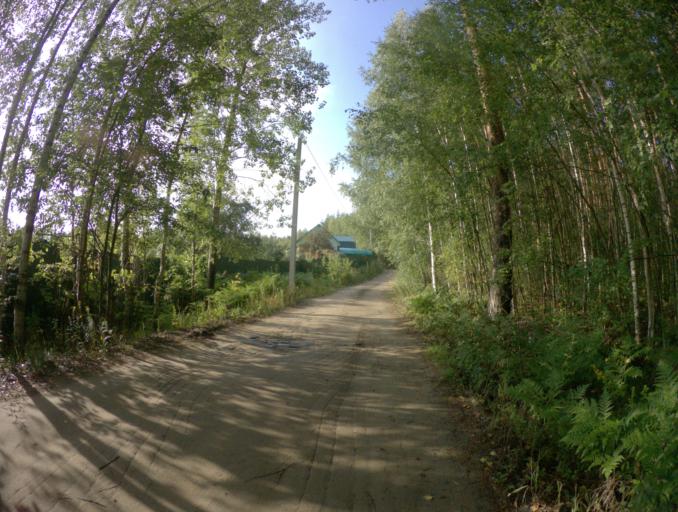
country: RU
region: Vladimir
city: Raduzhnyy
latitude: 56.0077
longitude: 40.2727
